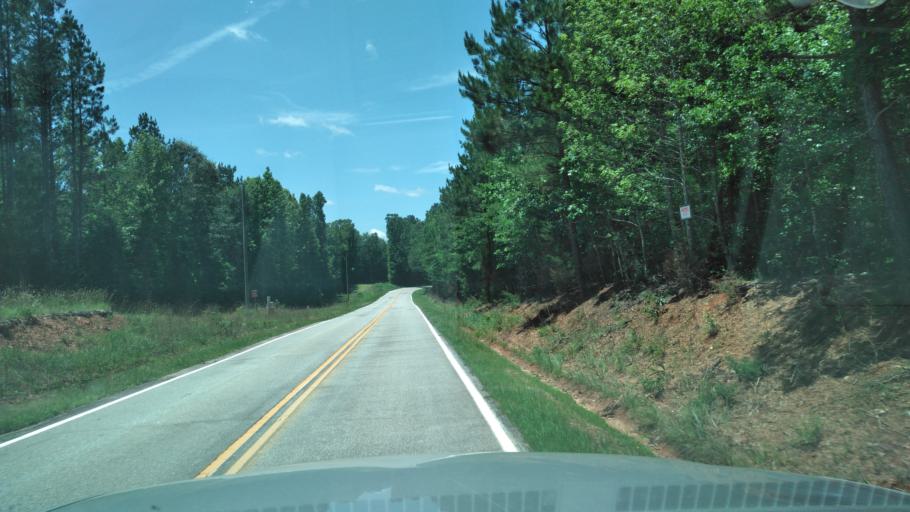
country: US
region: South Carolina
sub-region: Laurens County
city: Laurens
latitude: 34.3791
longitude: -82.0971
